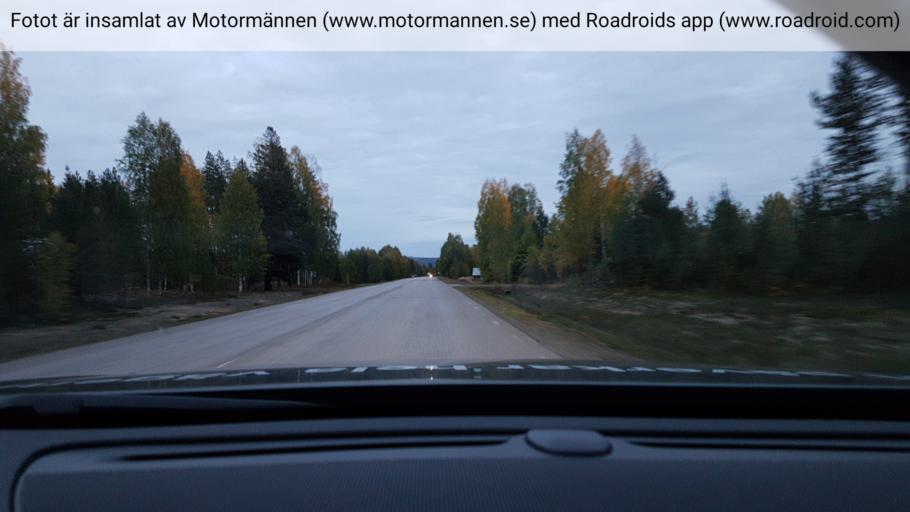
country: SE
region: Norrbotten
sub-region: Alvsbyns Kommun
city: AElvsbyn
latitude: 65.8464
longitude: 20.4720
